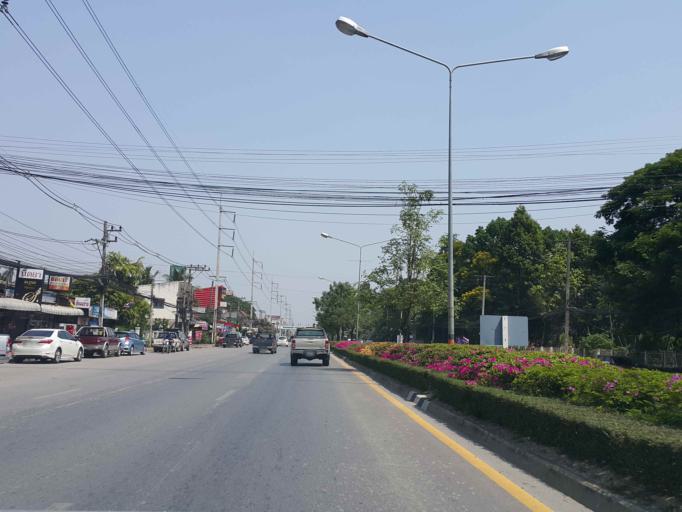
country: TH
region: Chiang Mai
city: San Sai
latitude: 18.8981
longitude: 99.0076
